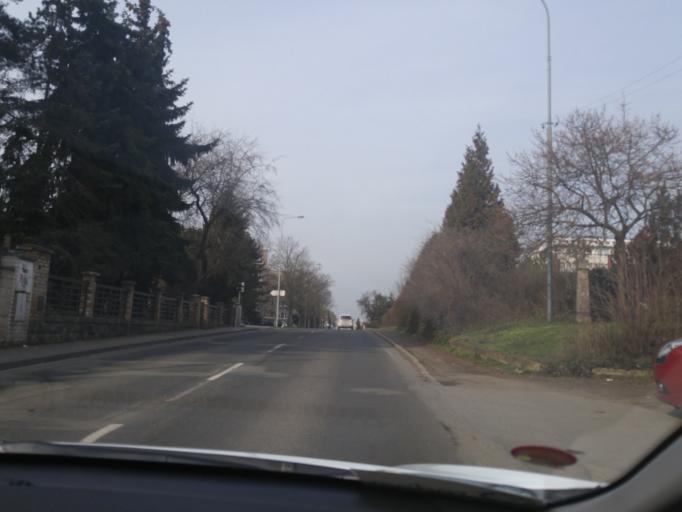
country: CZ
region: Central Bohemia
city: Brandys nad Labem-Stara Boleslav
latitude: 50.1889
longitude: 14.6527
